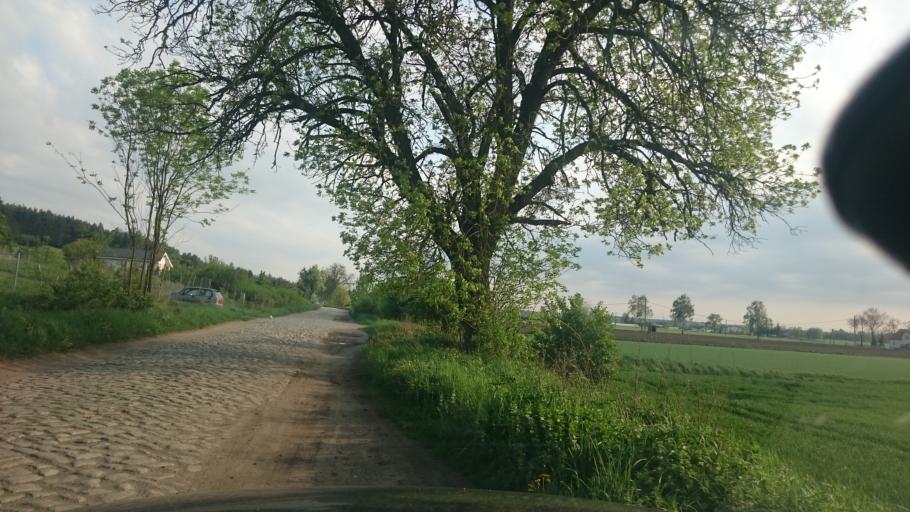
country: PL
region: Kujawsko-Pomorskie
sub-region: Grudziadz
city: Grudziadz
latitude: 53.4765
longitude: 18.8136
